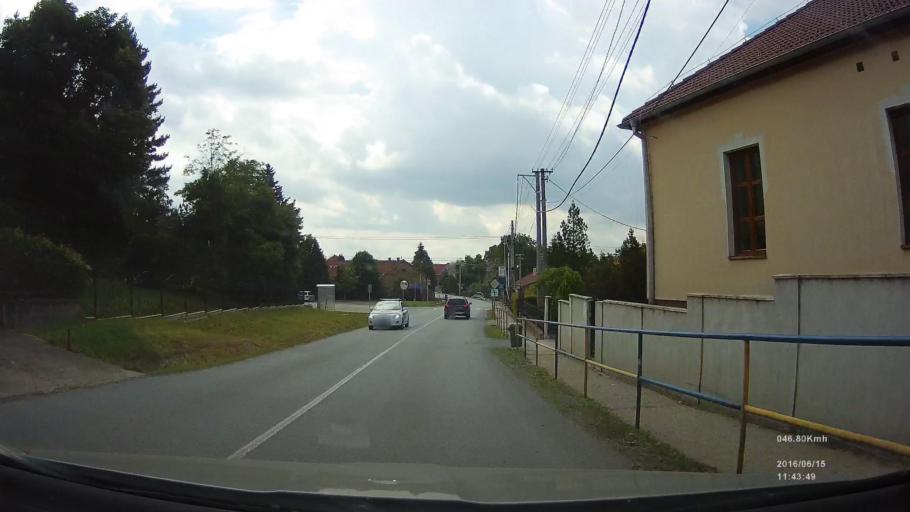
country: SK
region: Kosicky
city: Kosice
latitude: 48.7493
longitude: 21.3447
